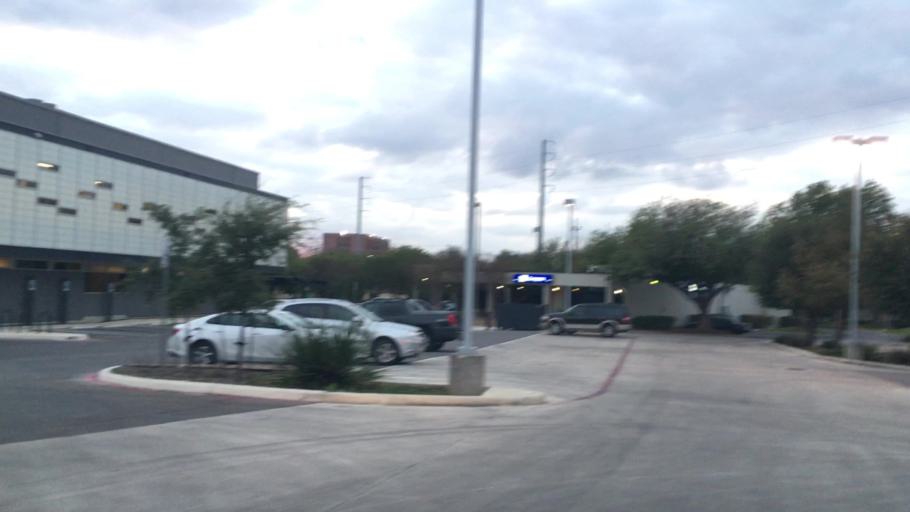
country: US
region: Texas
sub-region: Bexar County
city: Balcones Heights
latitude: 29.4885
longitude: -98.5731
